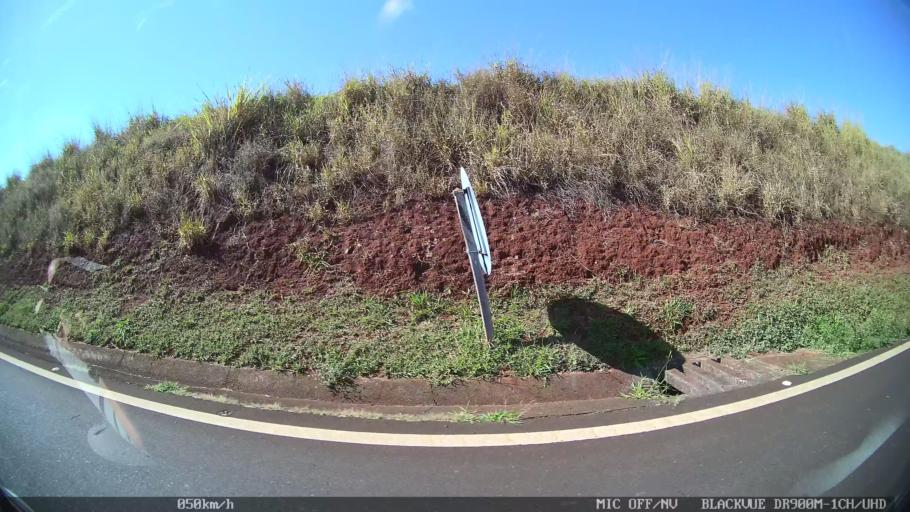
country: BR
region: Sao Paulo
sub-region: Franca
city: Franca
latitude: -20.6790
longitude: -47.4957
